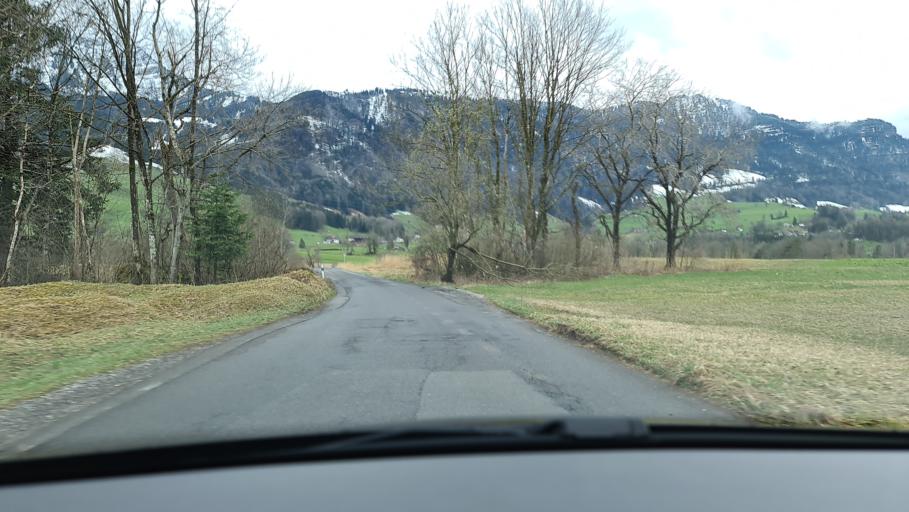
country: CH
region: Schwyz
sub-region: Bezirk Schwyz
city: Goldau
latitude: 47.0439
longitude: 8.5789
